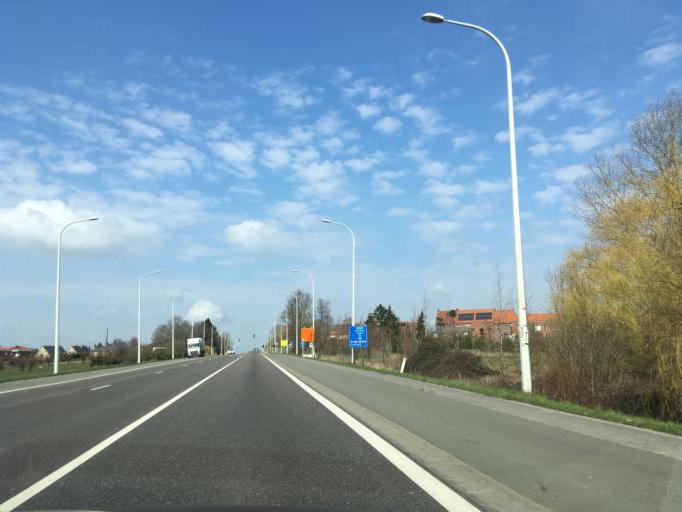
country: BE
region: Flanders
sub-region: Provincie West-Vlaanderen
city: Lendelede
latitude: 50.8849
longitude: 3.2589
